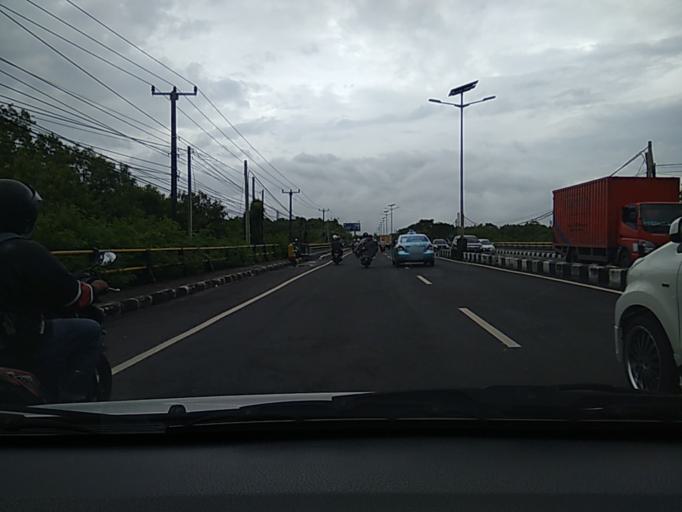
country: ID
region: Bali
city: Jimbaran
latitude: -8.7755
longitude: 115.1777
